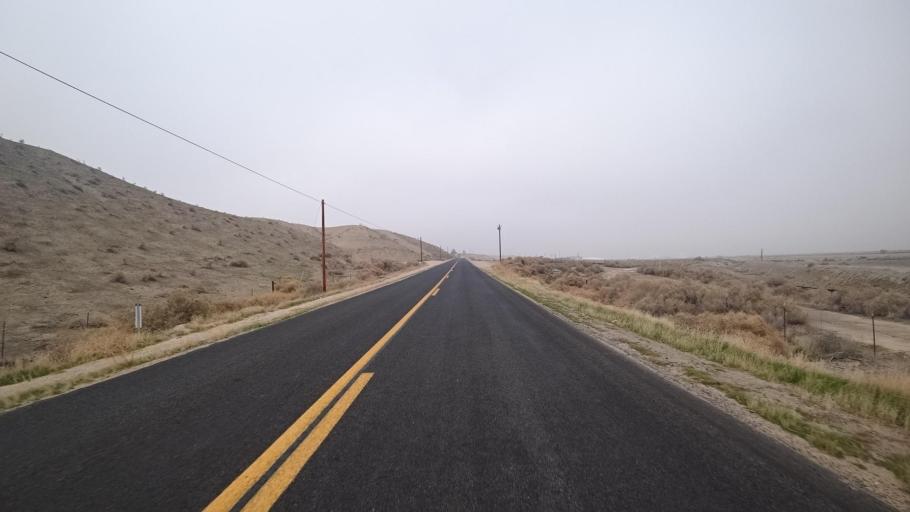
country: US
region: California
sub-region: Kern County
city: Ford City
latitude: 35.2585
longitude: -119.3098
